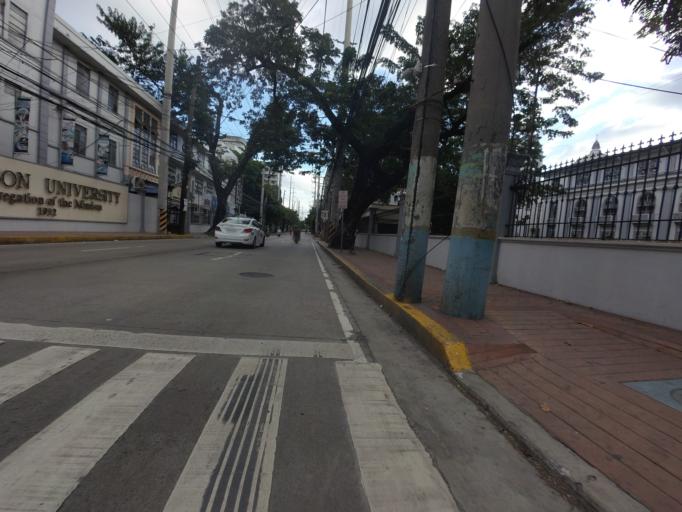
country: PH
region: Metro Manila
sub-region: City of Manila
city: Quiapo
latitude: 14.5860
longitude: 120.9858
